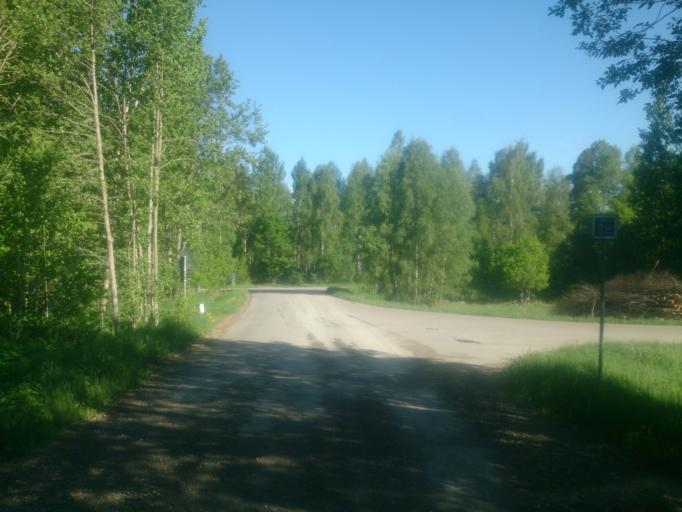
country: SE
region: OEstergoetland
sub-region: Atvidabergs Kommun
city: Atvidaberg
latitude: 58.2204
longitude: 15.9791
